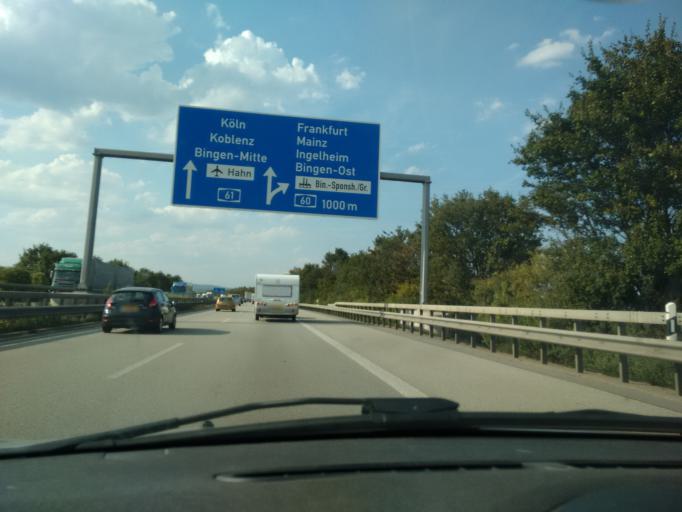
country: DE
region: Rheinland-Pfalz
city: Gensingen
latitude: 49.9149
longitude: 7.9491
